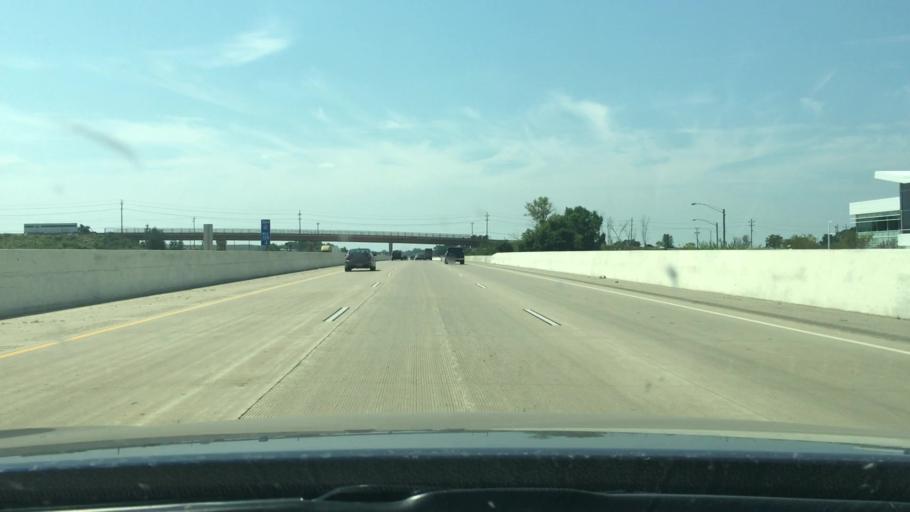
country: US
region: Wisconsin
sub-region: Winnebago County
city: Neenah
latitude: 44.1449
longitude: -88.4891
